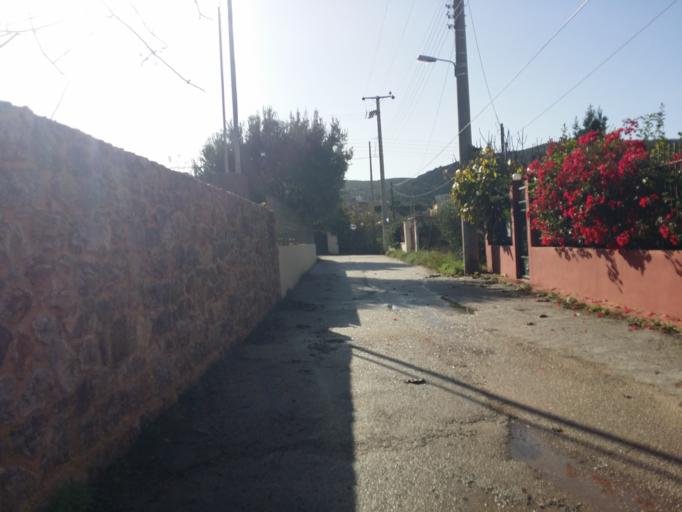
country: GR
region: Attica
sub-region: Nomarchia Anatolikis Attikis
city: Palaia Fokaia
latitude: 37.7167
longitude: 23.9617
